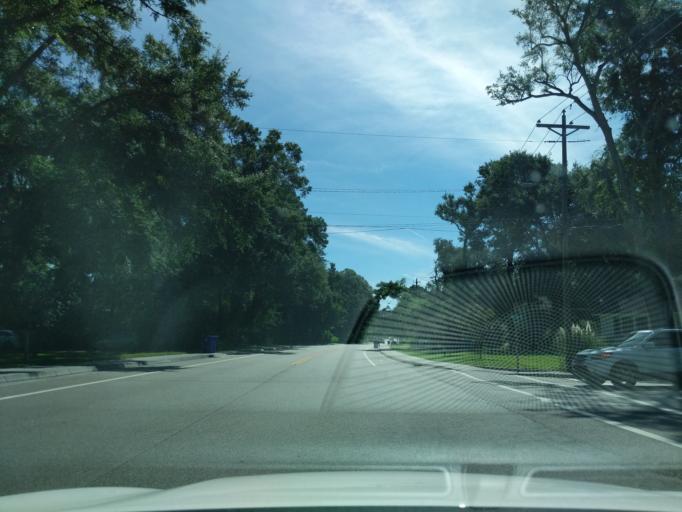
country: US
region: South Carolina
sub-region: Charleston County
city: Charleston
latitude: 32.7418
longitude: -79.9206
